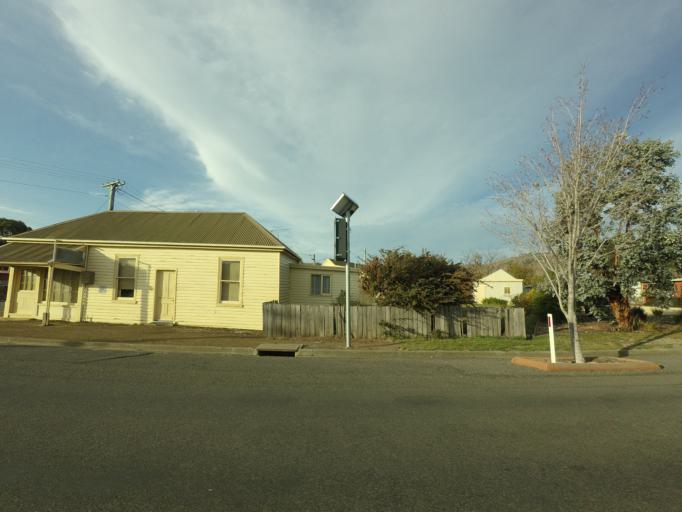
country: AU
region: Tasmania
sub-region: Brighton
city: Bridgewater
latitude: -42.5303
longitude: 147.2001
